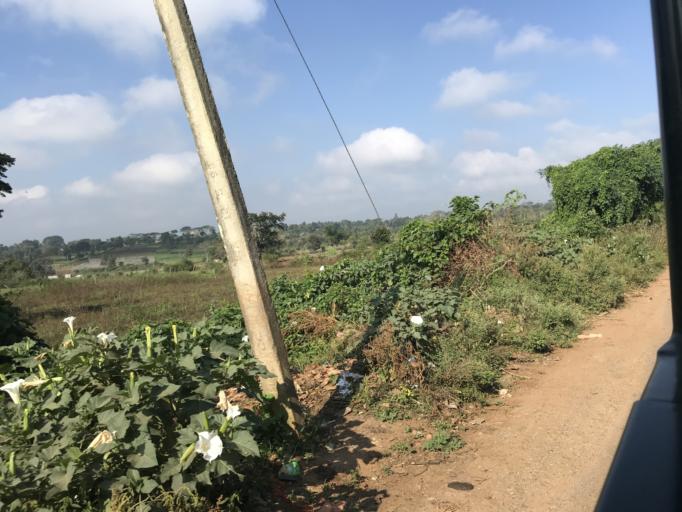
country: IN
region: Karnataka
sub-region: Mysore
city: Sargur
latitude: 11.9446
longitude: 76.2662
